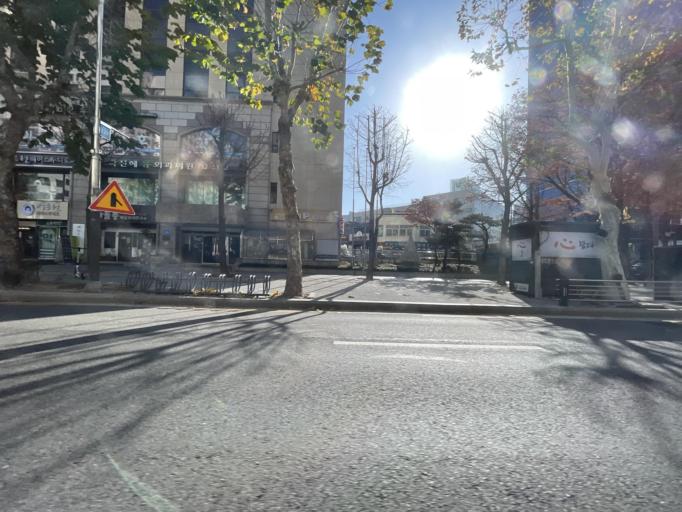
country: KR
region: Seoul
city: Seoul
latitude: 37.5400
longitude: 126.9468
